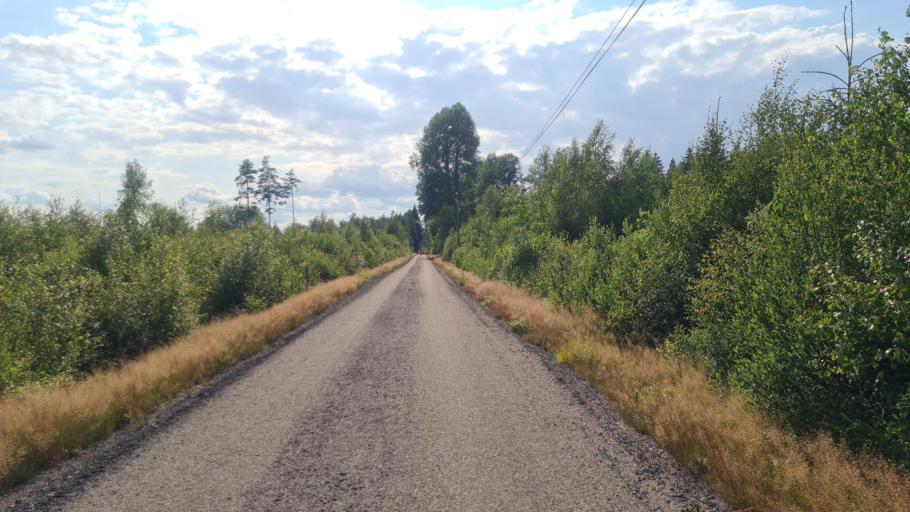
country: SE
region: Kronoberg
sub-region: Ljungby Kommun
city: Lagan
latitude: 56.8575
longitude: 14.1276
